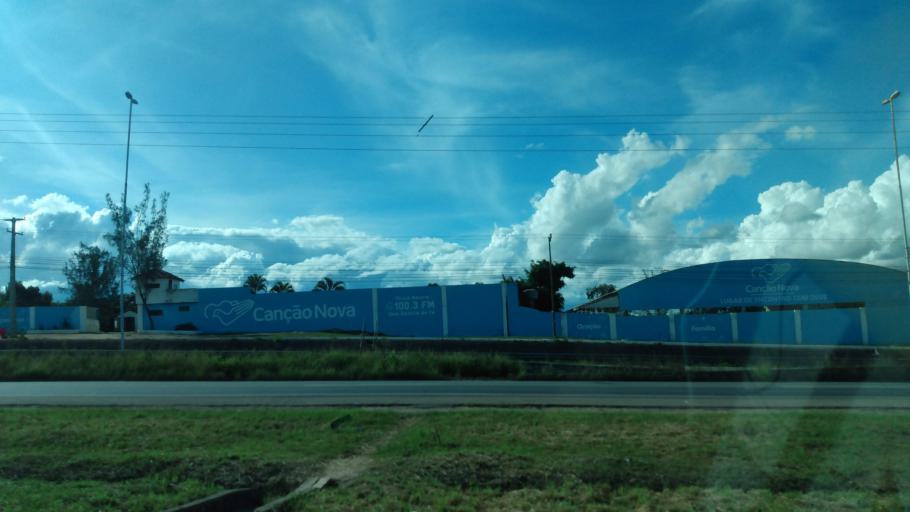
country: ET
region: Oromiya
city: Gore
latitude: 8.1978
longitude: 35.5819
